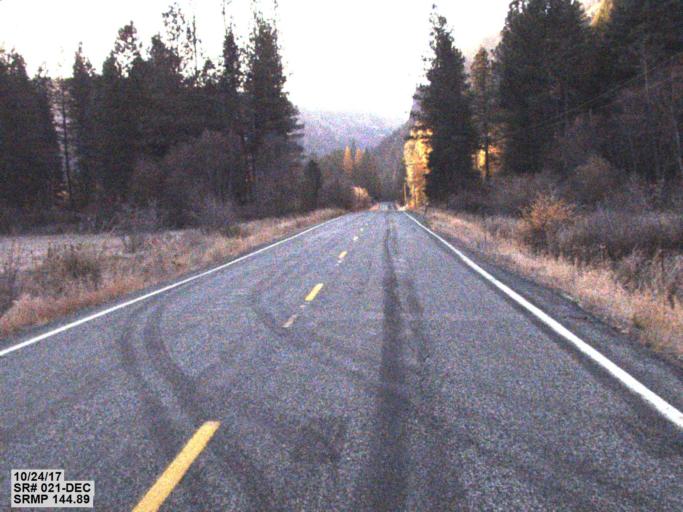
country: US
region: Washington
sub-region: Ferry County
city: Republic
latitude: 48.4489
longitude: -118.7450
